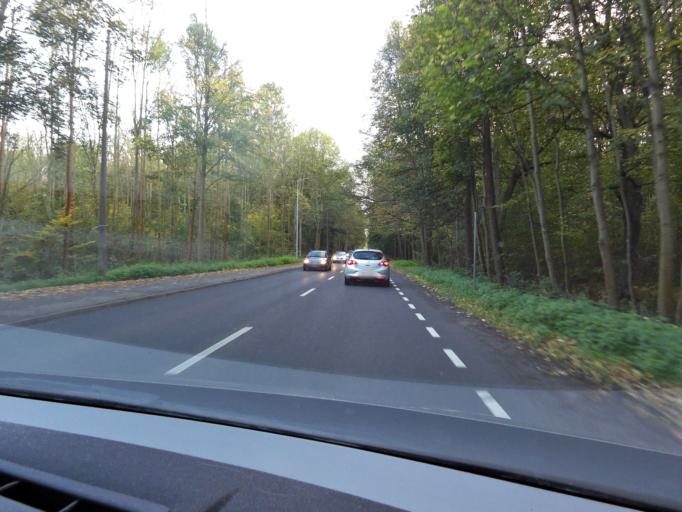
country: DE
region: Saxony
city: Leipzig
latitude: 51.3636
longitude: 12.3138
